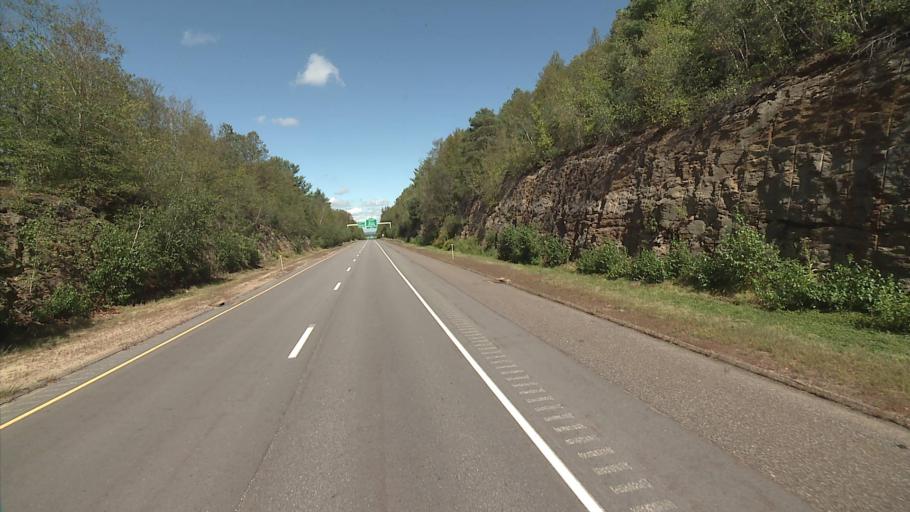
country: US
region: Connecticut
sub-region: New London County
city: Colchester
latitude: 41.5466
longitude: -72.3158
